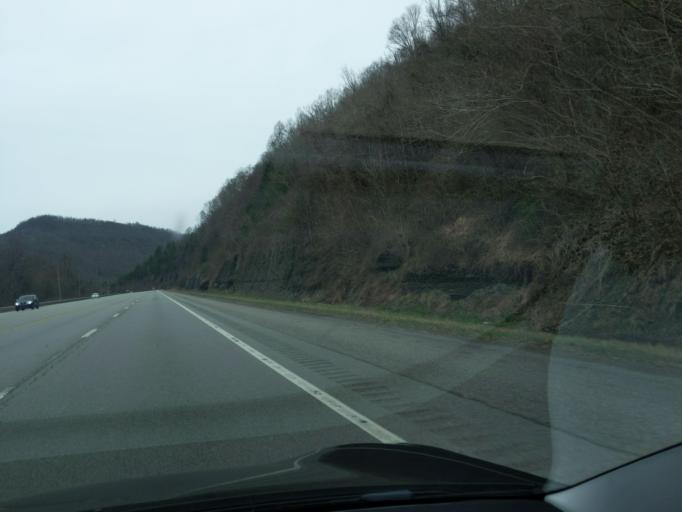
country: US
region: Kentucky
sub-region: Bell County
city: Pineville
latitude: 36.7813
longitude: -83.7390
